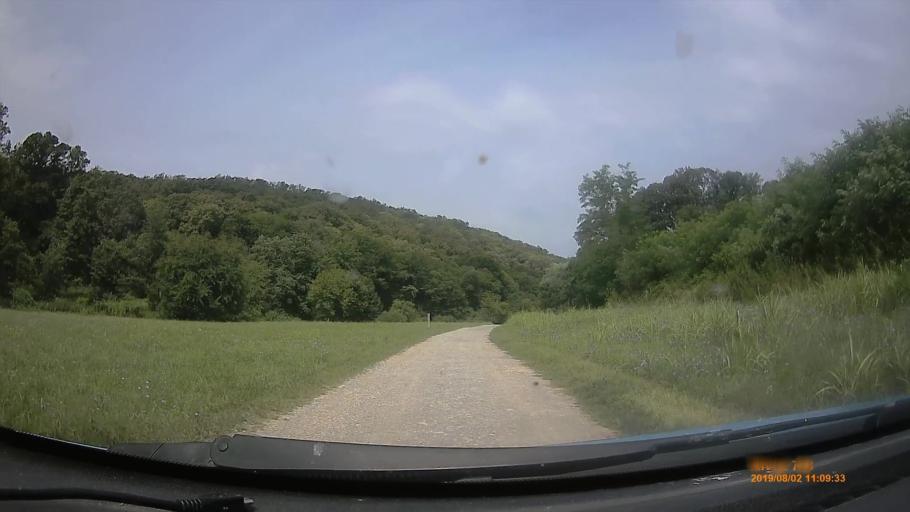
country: HU
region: Baranya
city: Buekkoesd
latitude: 46.1027
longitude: 17.9397
